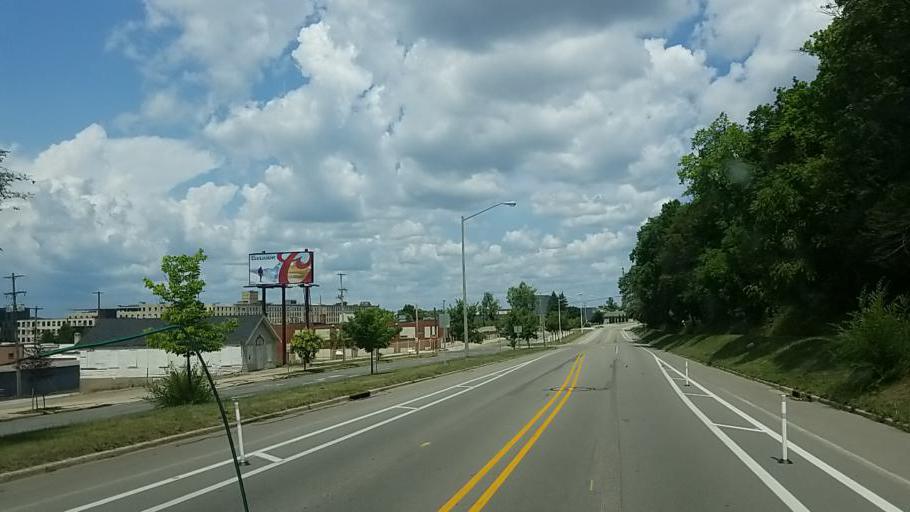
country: US
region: Michigan
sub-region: Kent County
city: Grand Rapids
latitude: 42.9757
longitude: -85.6689
